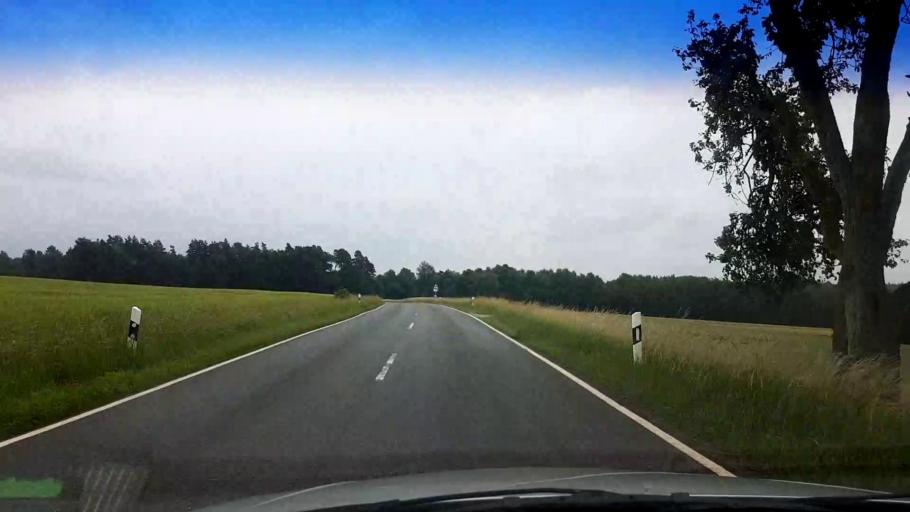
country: DE
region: Bavaria
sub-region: Upper Franconia
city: Weismain
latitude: 50.0861
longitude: 11.2880
